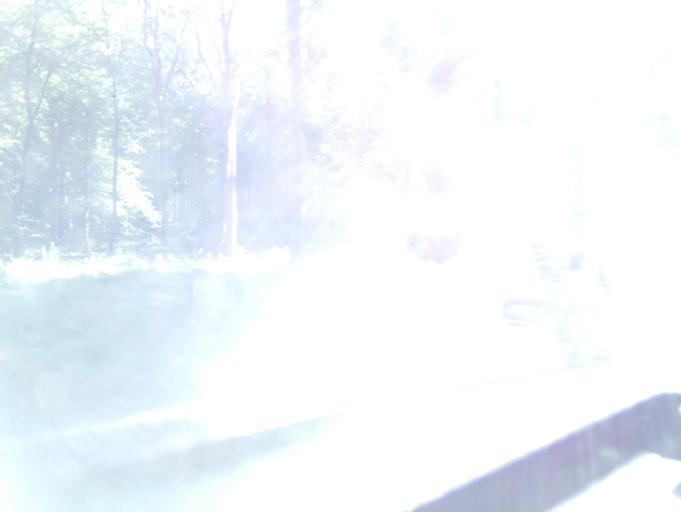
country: GB
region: England
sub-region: Gloucestershire
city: Cinderford
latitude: 51.7826
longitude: -2.4993
